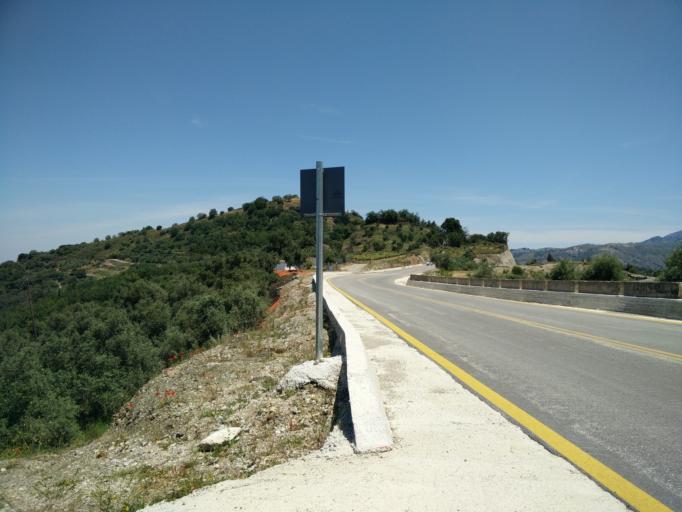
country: GR
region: Crete
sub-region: Nomos Chanias
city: Galatas
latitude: 35.3930
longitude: 23.9286
